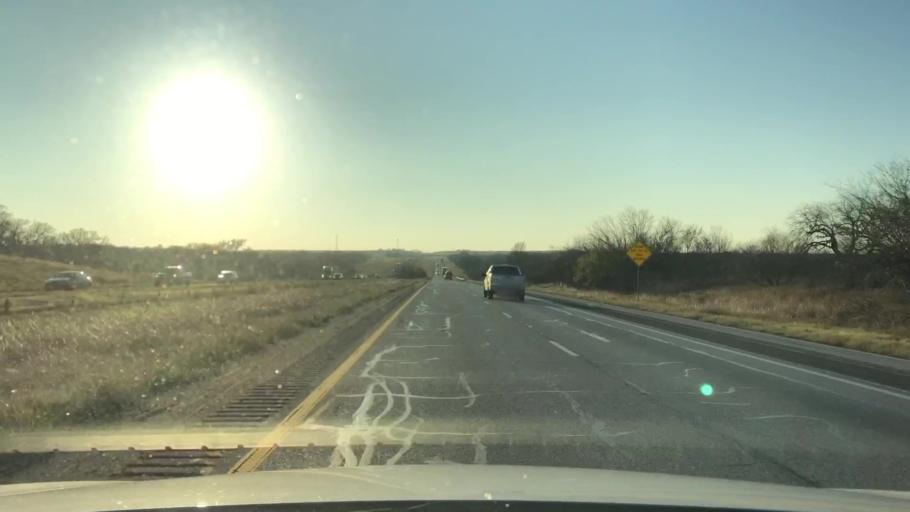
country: US
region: Texas
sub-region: Caldwell County
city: Luling
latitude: 29.6353
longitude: -97.7339
